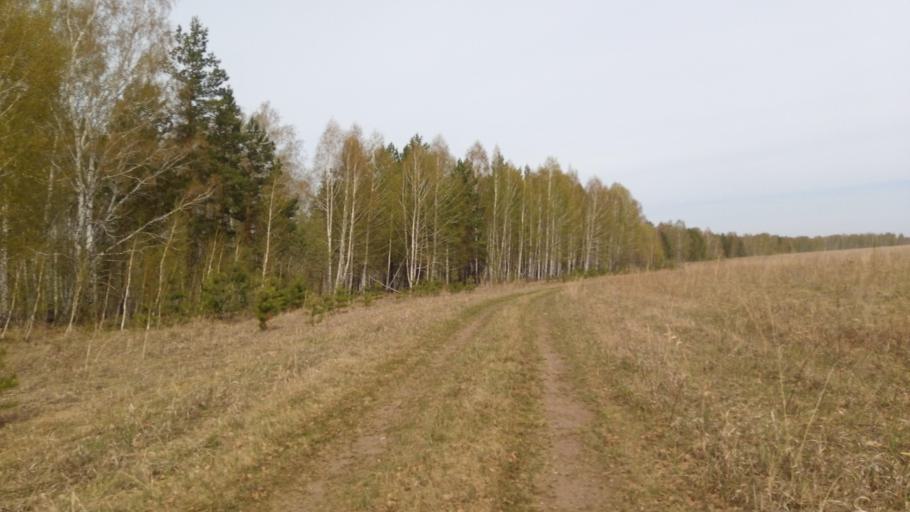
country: RU
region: Chelyabinsk
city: Timiryazevskiy
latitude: 55.0158
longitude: 60.8625
